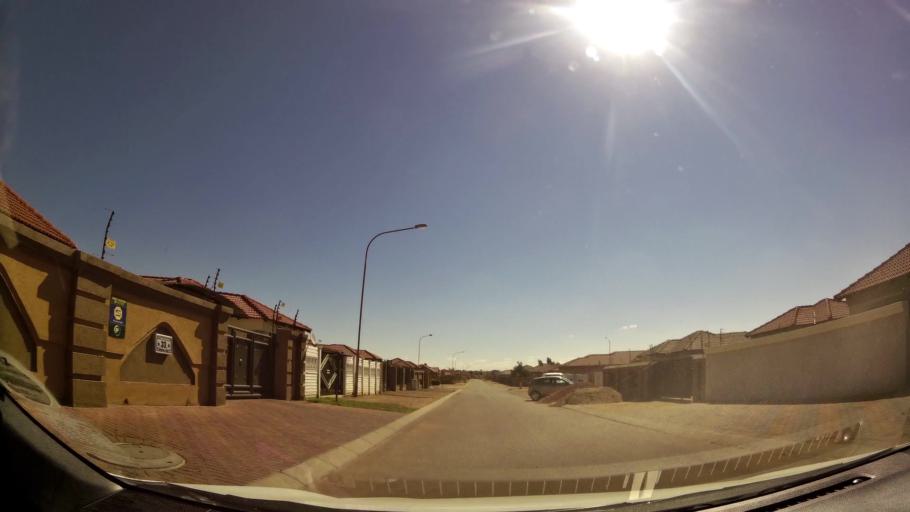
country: ZA
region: Limpopo
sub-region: Capricorn District Municipality
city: Polokwane
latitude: -23.8655
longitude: 29.4262
